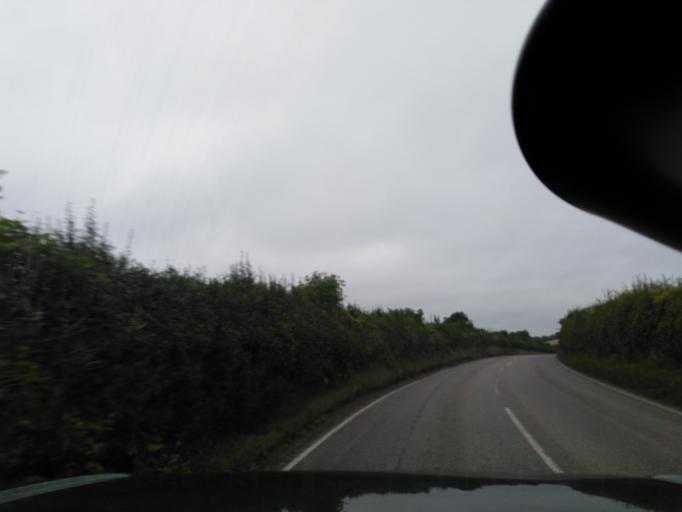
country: GB
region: England
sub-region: Dorset
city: Blandford Forum
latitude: 50.9137
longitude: -2.1956
